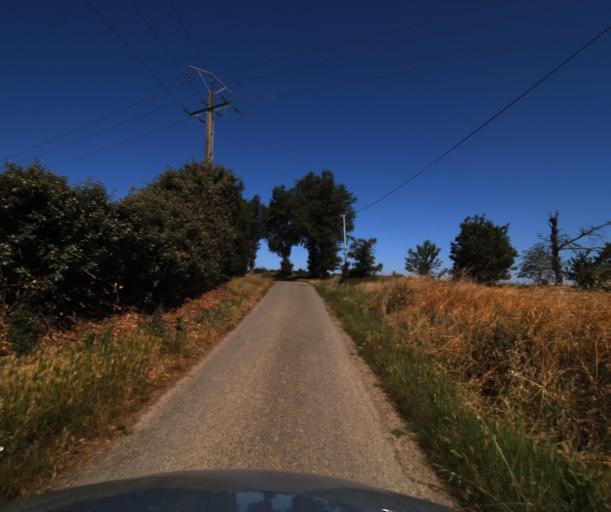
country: FR
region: Midi-Pyrenees
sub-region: Departement de la Haute-Garonne
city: Muret
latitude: 43.4543
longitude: 1.3632
